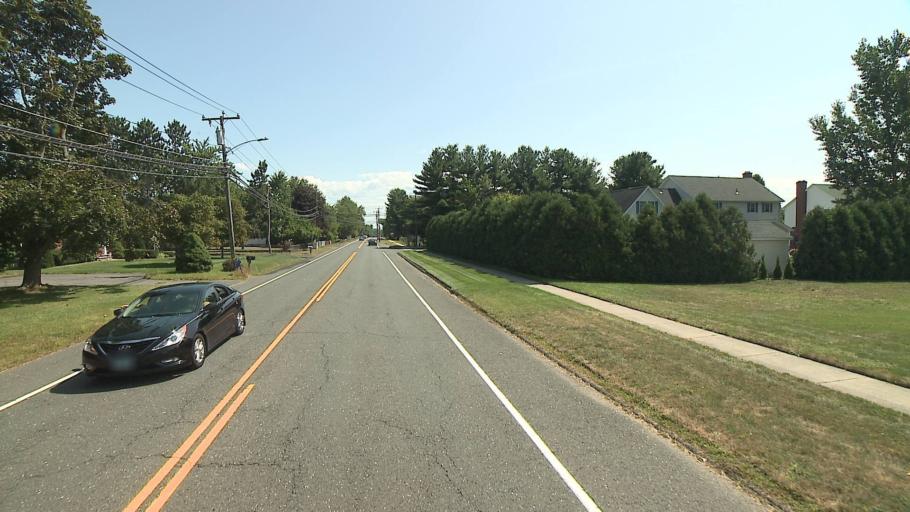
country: US
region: Connecticut
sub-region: Hartford County
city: Windsor Locks
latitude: 41.9265
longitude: -72.6532
